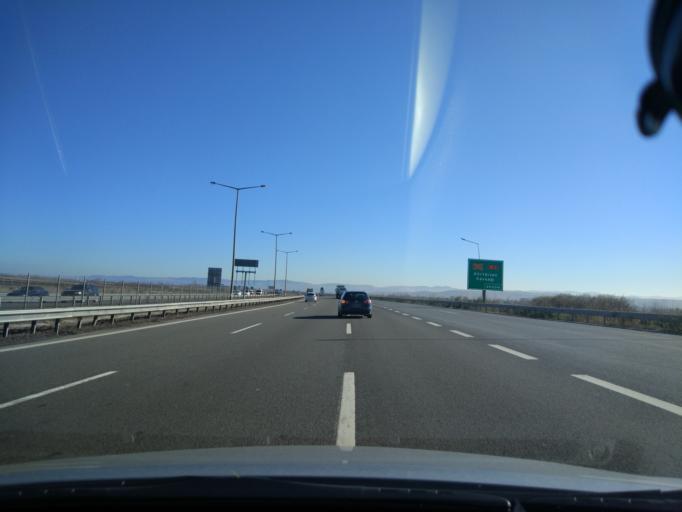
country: TR
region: Bolu
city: Dortdivan
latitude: 40.7480
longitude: 32.0881
